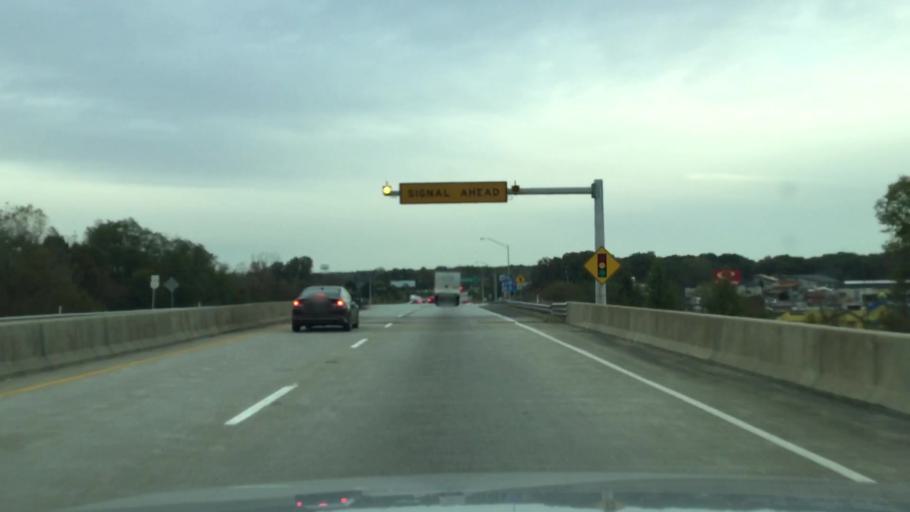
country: US
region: Indiana
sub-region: Porter County
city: Chesterton
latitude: 41.6196
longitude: -87.0432
